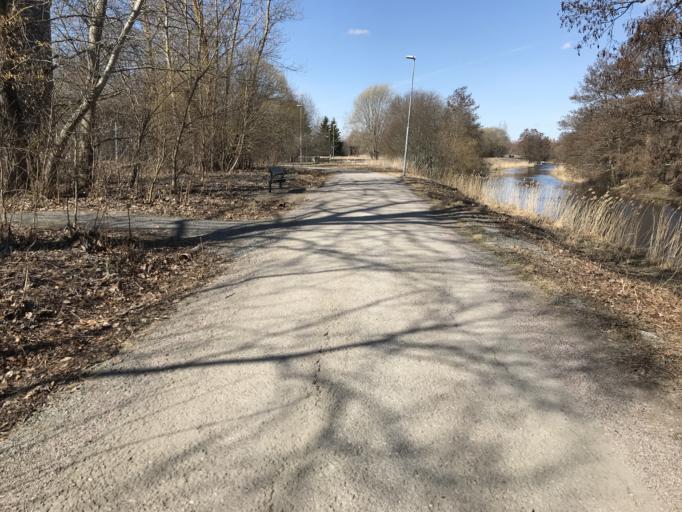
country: SE
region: Uppsala
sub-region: Uppsala Kommun
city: Uppsala
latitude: 59.8726
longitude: 17.6102
